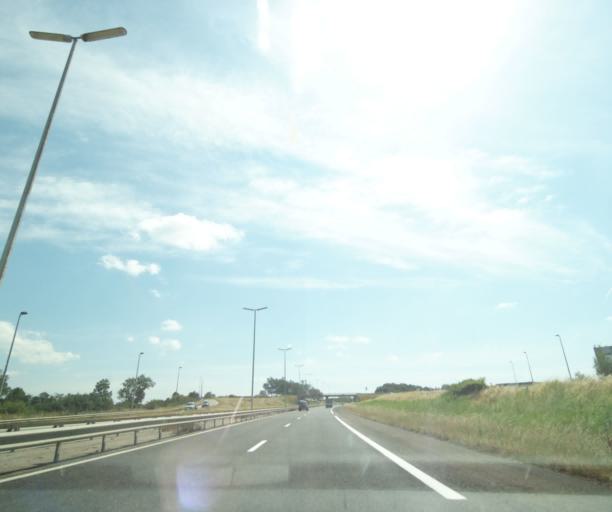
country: FR
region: Lorraine
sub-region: Departement de Meurthe-et-Moselle
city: Saint-Nicolas-de-Port
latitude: 48.6191
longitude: 6.2721
